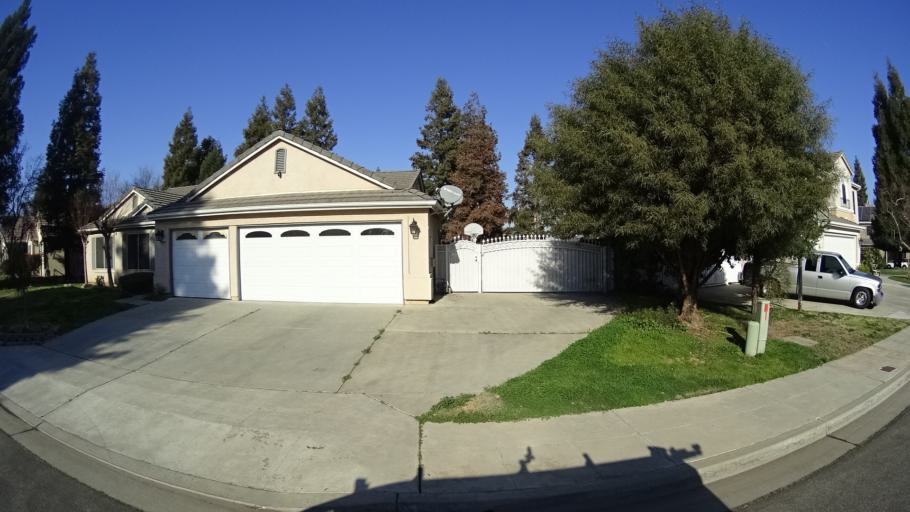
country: US
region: California
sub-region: Fresno County
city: Clovis
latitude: 36.8695
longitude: -119.7358
